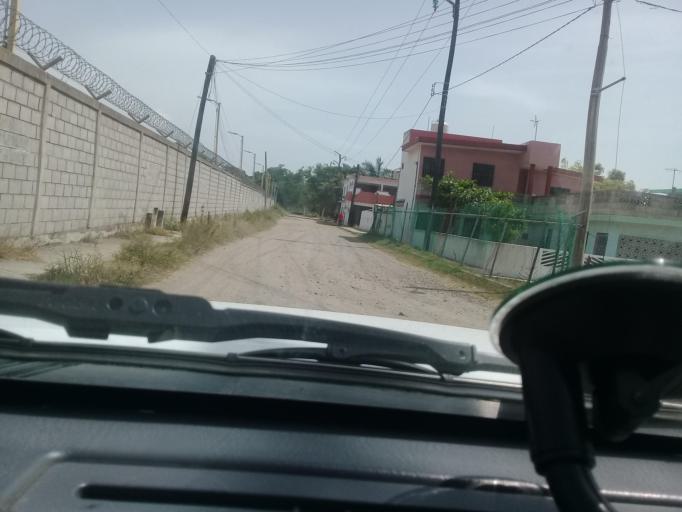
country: MX
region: Veracruz
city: Anahuac
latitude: 22.2296
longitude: -97.8324
